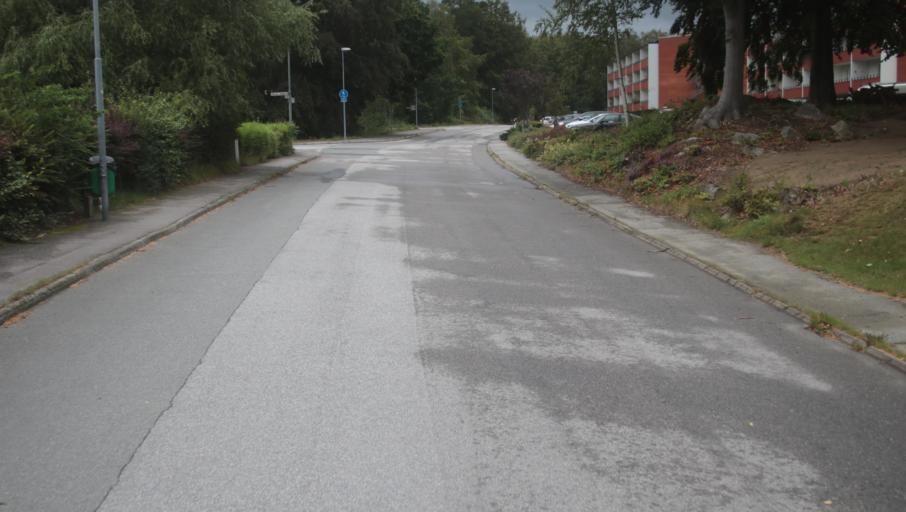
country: SE
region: Blekinge
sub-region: Karlshamns Kommun
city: Svangsta
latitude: 56.2597
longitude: 14.7799
